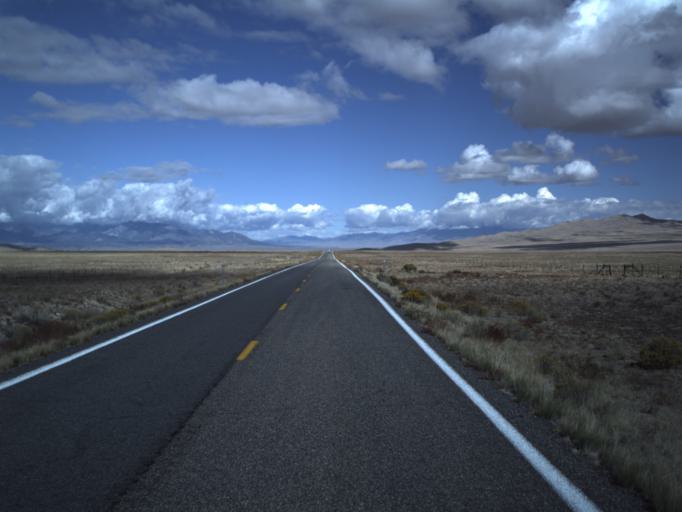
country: US
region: Utah
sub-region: Beaver County
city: Milford
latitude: 38.6616
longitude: -113.8777
